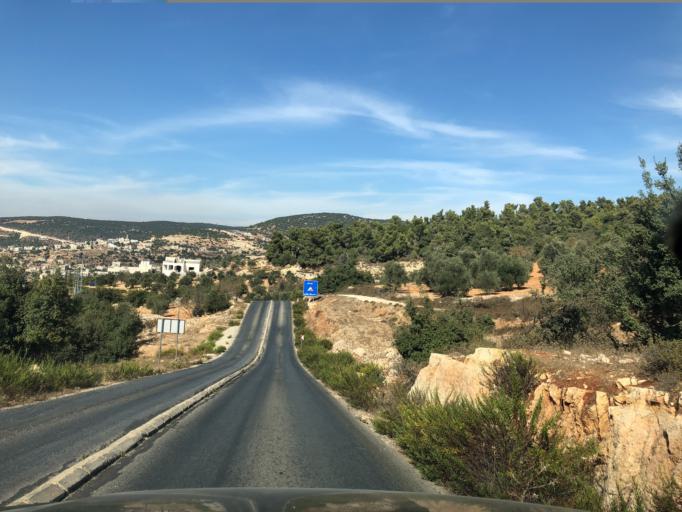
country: JO
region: Irbid
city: `Ayn Jannah
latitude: 32.3227
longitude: 35.7607
